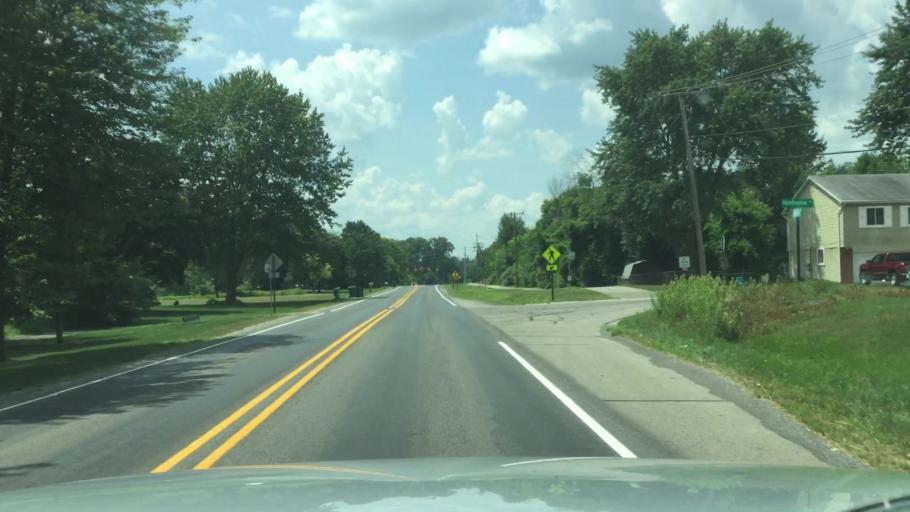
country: US
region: Michigan
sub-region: Washtenaw County
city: Ypsilanti
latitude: 42.2026
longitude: -83.6057
